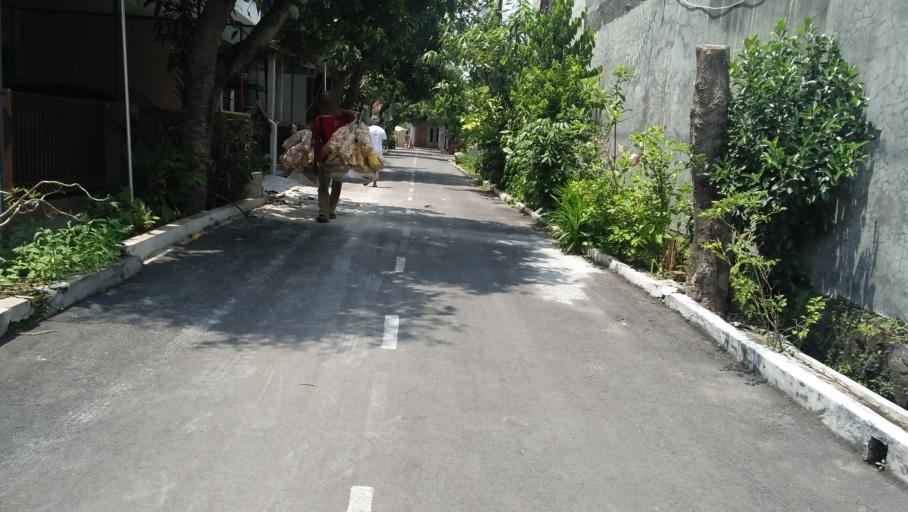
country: ID
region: Central Java
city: Mranggen
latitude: -7.0278
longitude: 110.4630
